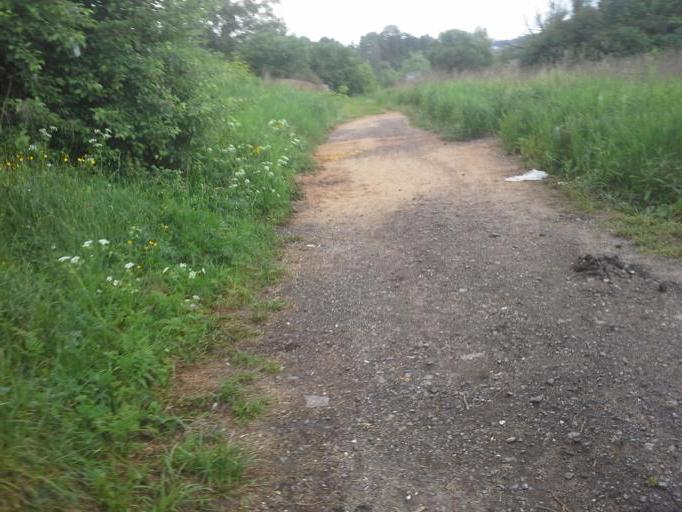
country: RU
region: Moskovskaya
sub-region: Leninskiy Rayon
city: Vnukovo
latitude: 55.6189
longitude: 37.3029
